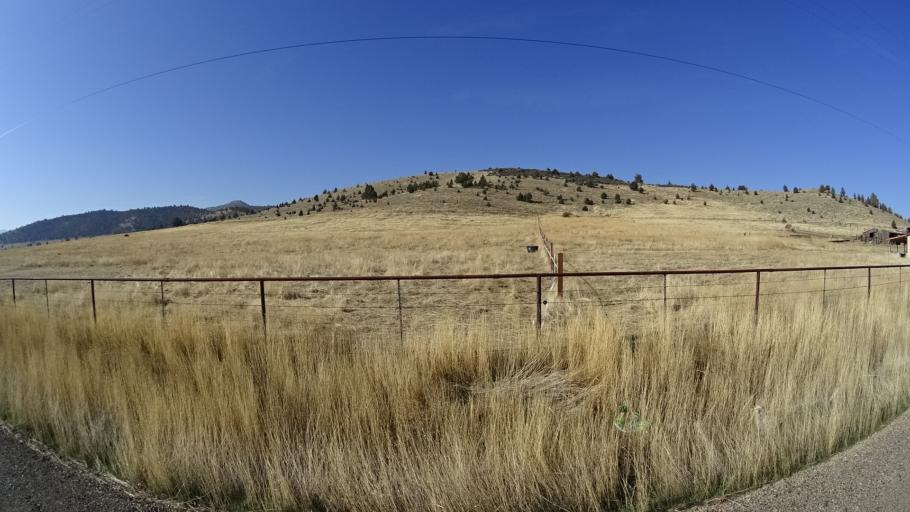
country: US
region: California
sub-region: Siskiyou County
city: Montague
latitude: 41.6401
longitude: -122.5330
